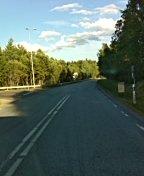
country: SE
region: Uppsala
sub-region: Habo Kommun
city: Balsta
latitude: 59.6526
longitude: 17.5571
